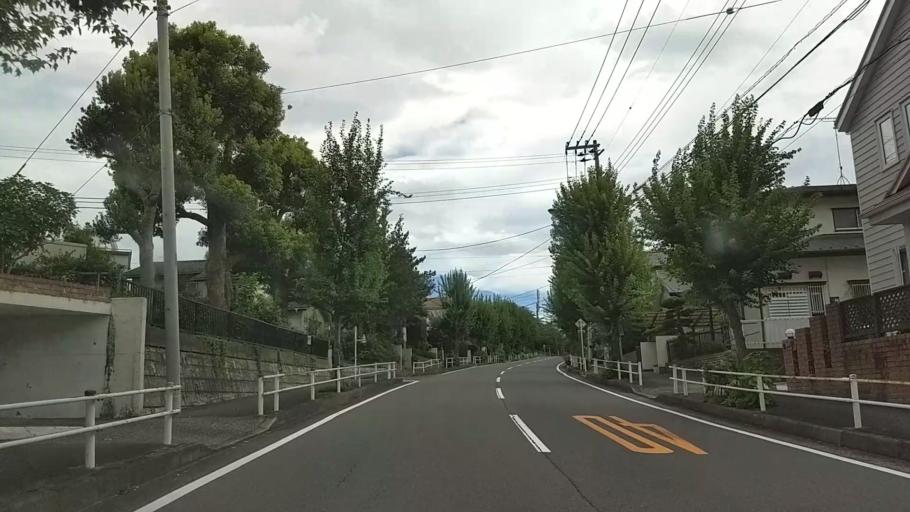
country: JP
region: Tokyo
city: Hachioji
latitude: 35.6327
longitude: 139.3579
